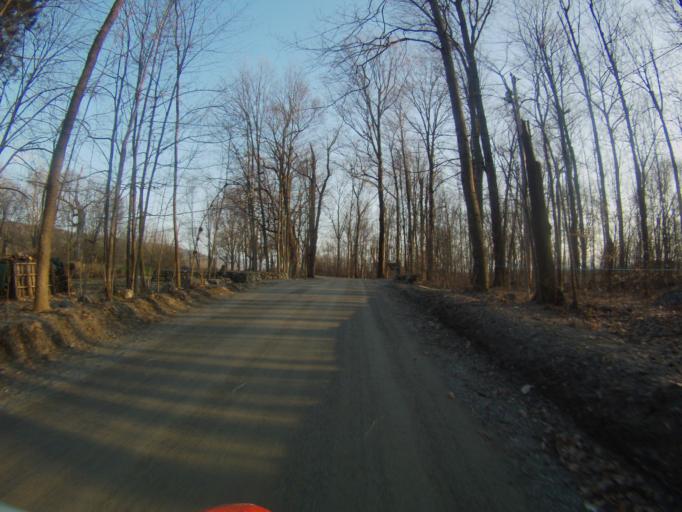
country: US
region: Vermont
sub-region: Addison County
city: Middlebury (village)
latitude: 44.0453
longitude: -73.1040
